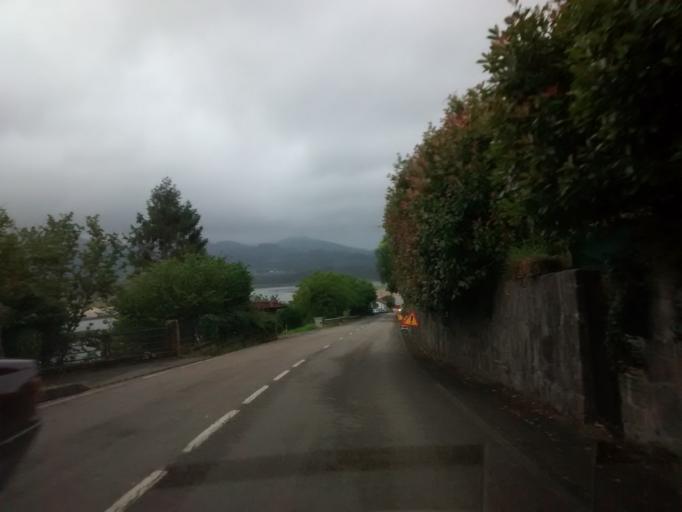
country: ES
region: Asturias
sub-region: Province of Asturias
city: Villaviciosa
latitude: 43.5277
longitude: -5.3905
